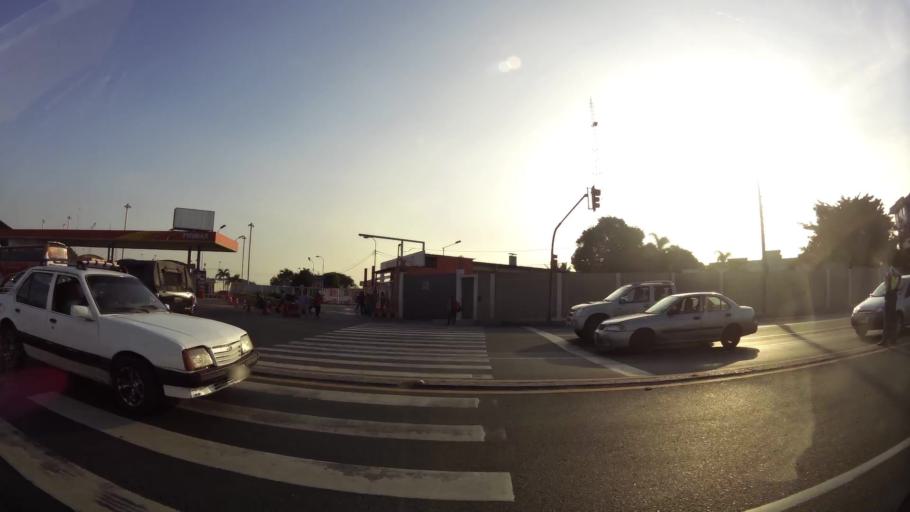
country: EC
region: Guayas
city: Eloy Alfaro
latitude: -2.1418
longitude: -79.8787
